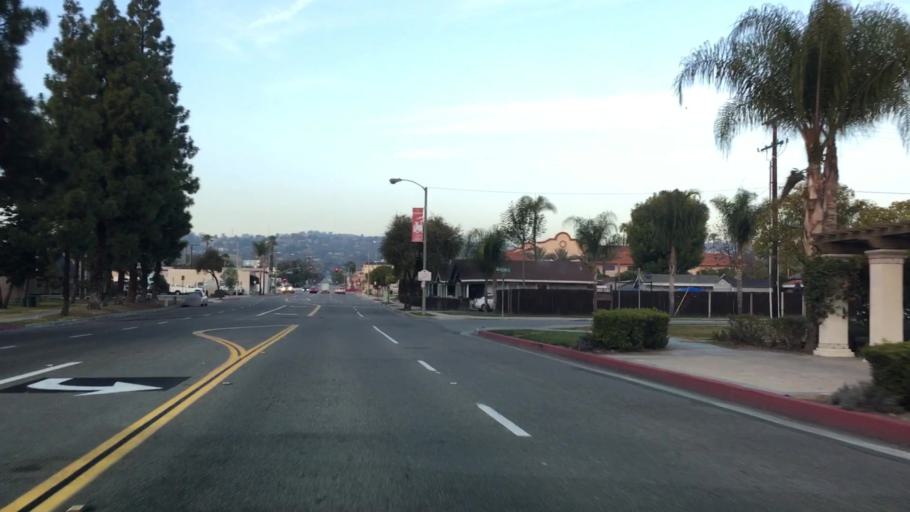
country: US
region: California
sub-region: Orange County
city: La Habra
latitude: 33.9296
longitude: -117.9461
